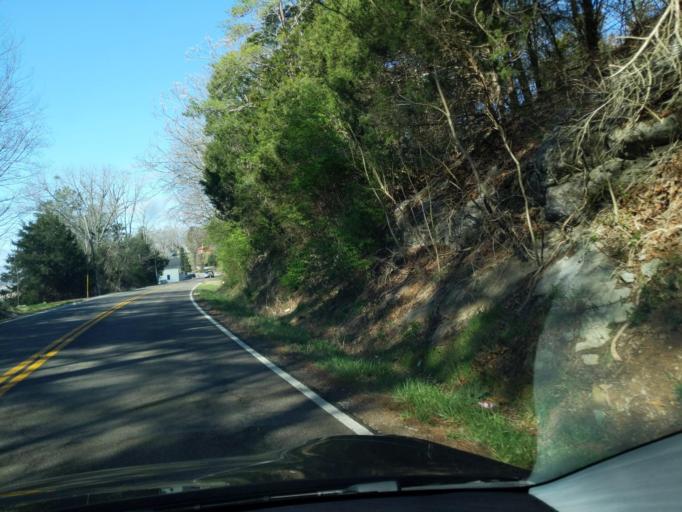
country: US
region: Tennessee
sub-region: Jefferson County
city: Dandridge
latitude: 35.9747
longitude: -83.4939
